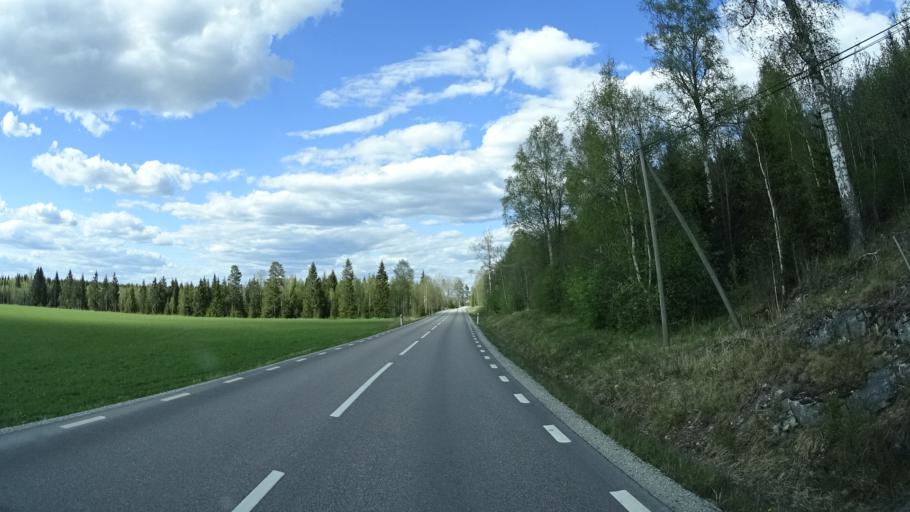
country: SE
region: OErebro
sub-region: Nora Kommun
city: As
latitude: 59.4597
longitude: 14.9012
